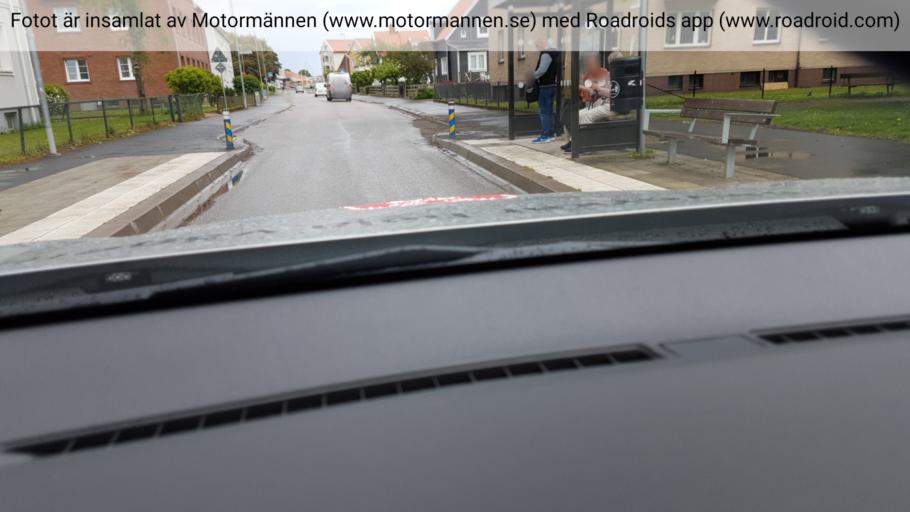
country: SE
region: Vaestra Goetaland
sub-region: Skovde Kommun
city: Skoevde
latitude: 58.3984
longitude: 13.8474
